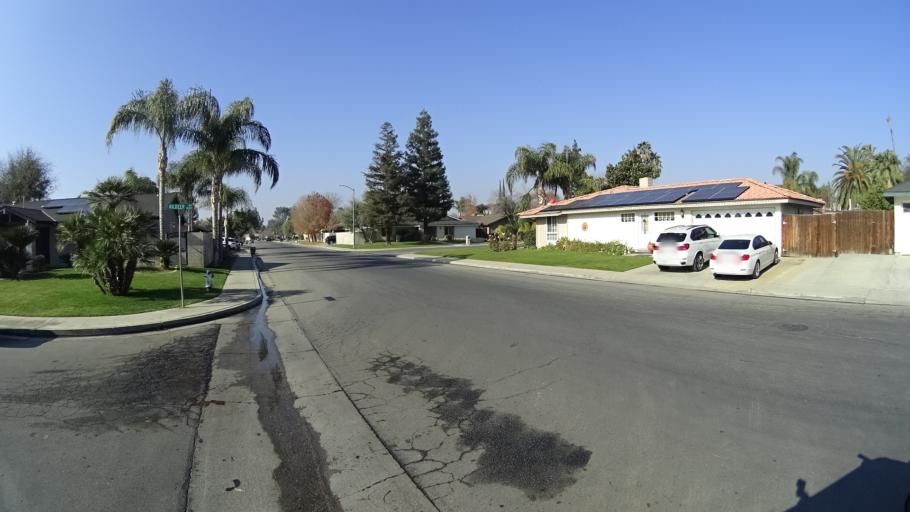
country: US
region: California
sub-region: Kern County
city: Greenacres
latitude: 35.3571
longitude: -119.0772
